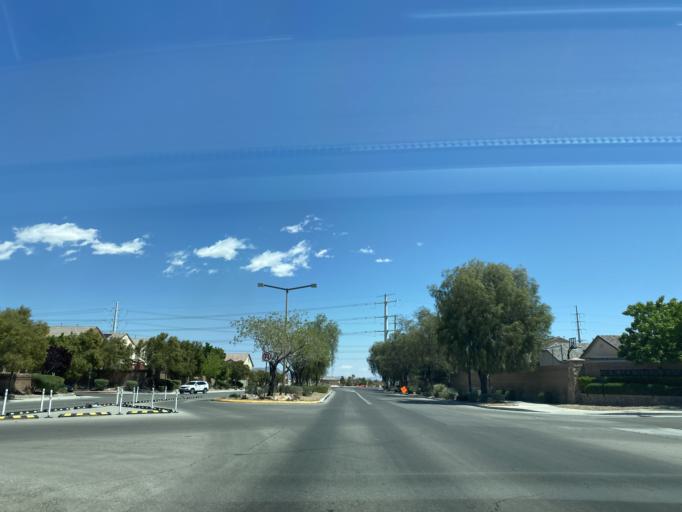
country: US
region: Nevada
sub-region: Clark County
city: North Las Vegas
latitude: 36.3059
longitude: -115.2097
